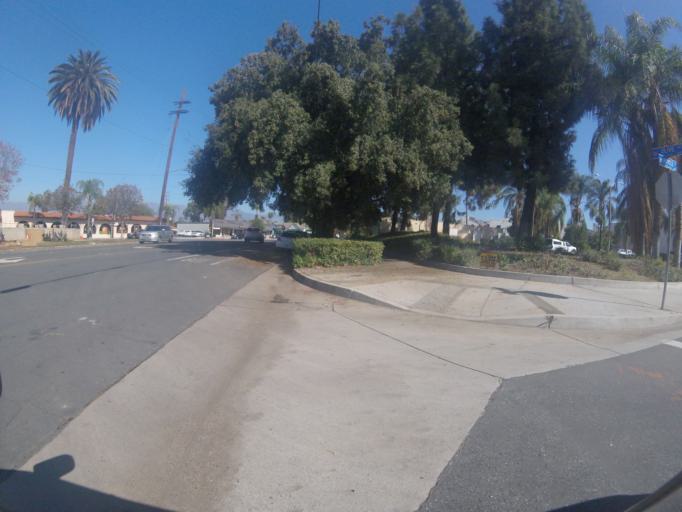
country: US
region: California
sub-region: San Bernardino County
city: Redlands
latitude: 34.0551
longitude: -117.1782
